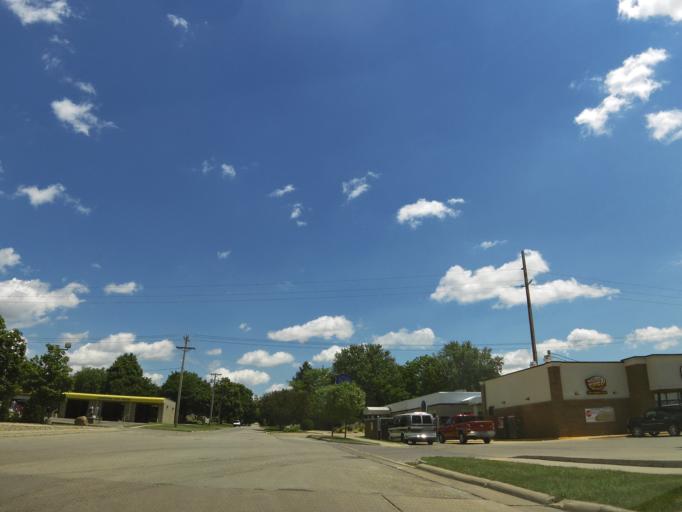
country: US
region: Iowa
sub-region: Fayette County
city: Oelwein
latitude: 42.6770
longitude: -91.9119
